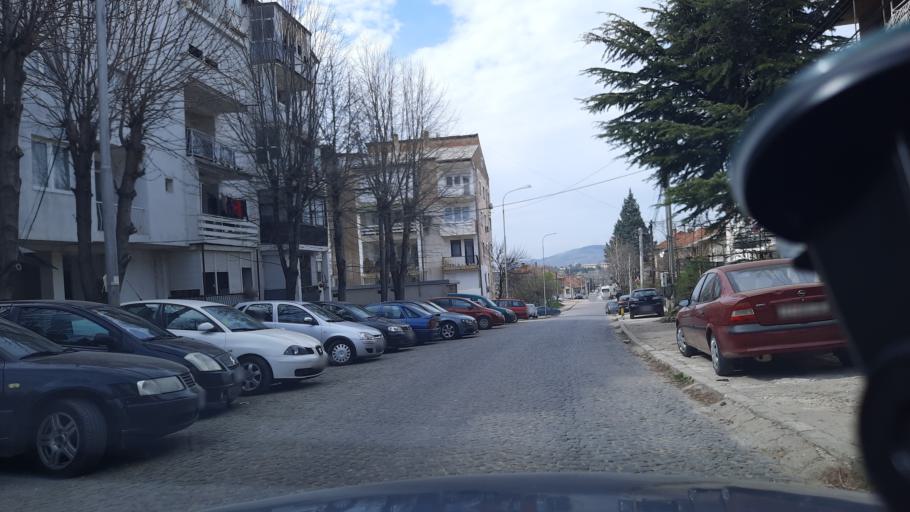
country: MK
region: Stip
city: Shtip
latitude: 41.7457
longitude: 22.1982
